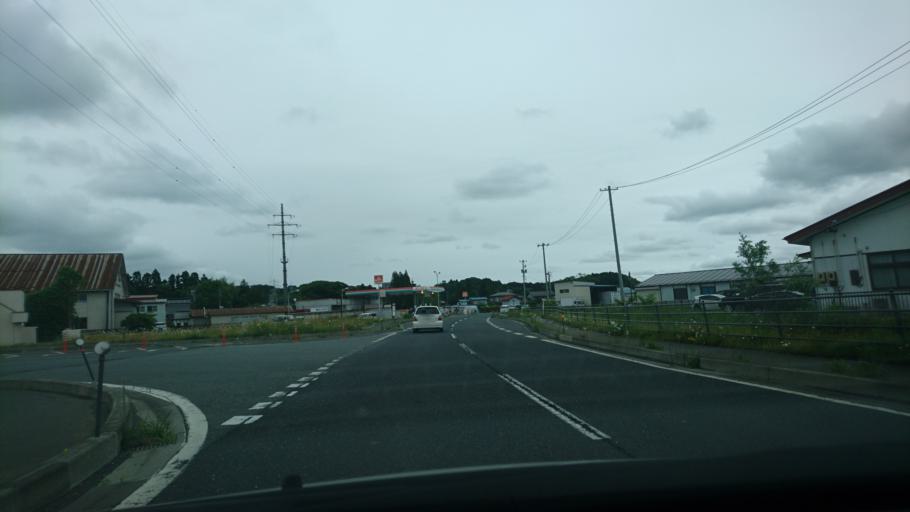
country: JP
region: Iwate
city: Ichinoseki
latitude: 39.0077
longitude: 141.1082
